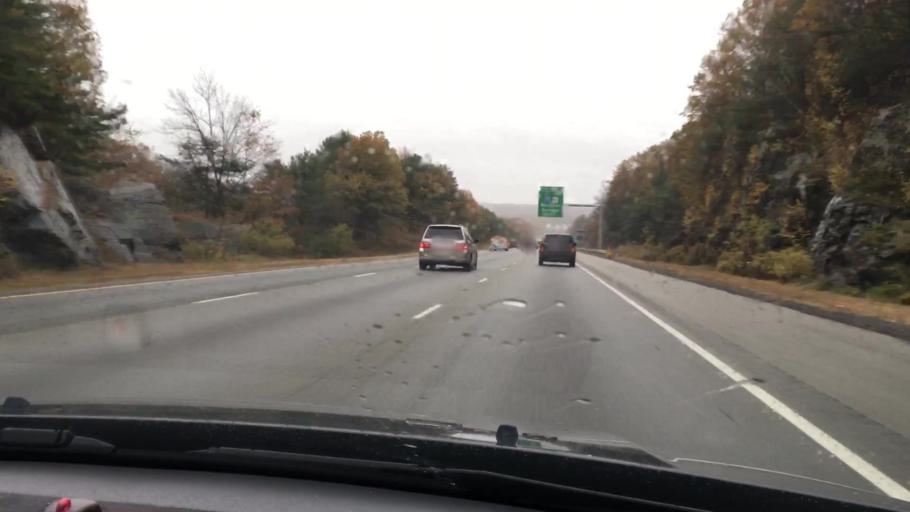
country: US
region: Massachusetts
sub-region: Worcester County
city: Berlin
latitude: 42.3791
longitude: -71.6006
